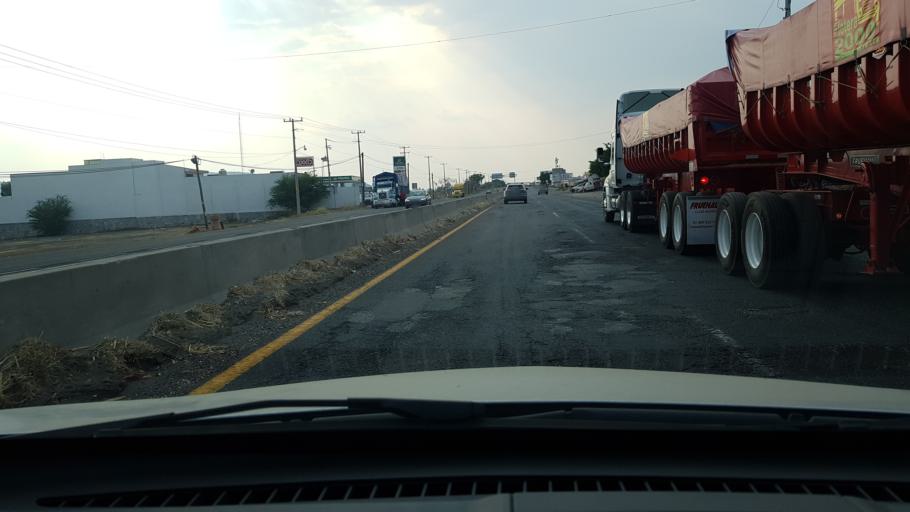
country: MX
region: Morelos
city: Amayuca
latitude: 18.7336
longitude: -98.8169
